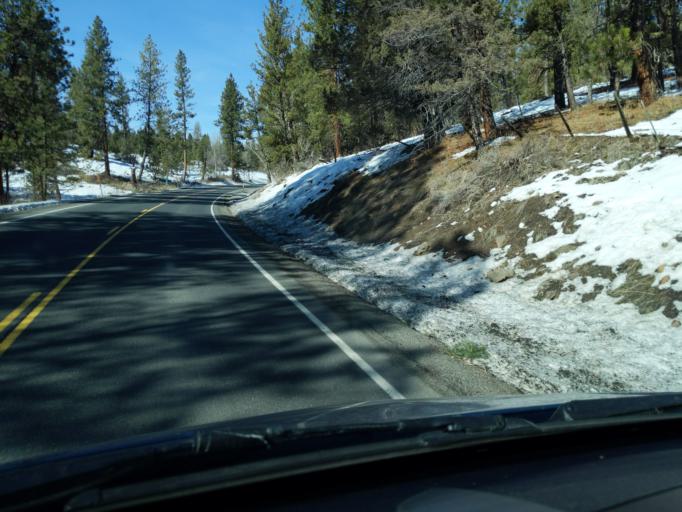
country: US
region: Oregon
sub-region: Grant County
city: John Day
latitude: 44.8942
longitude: -119.0142
